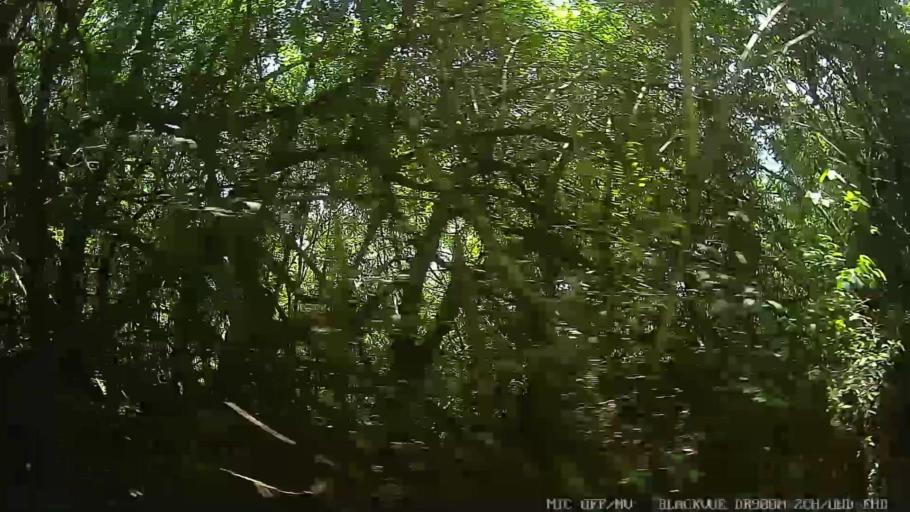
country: BR
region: Sao Paulo
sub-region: Atibaia
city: Atibaia
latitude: -23.0778
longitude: -46.6182
